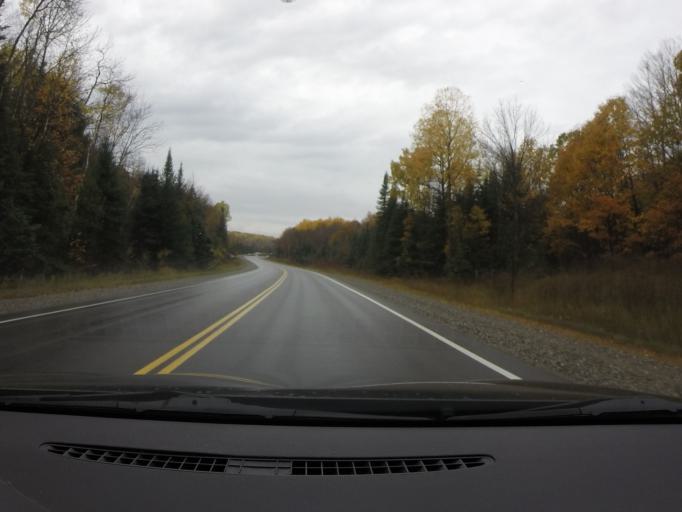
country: CA
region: Ontario
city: Perth
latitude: 44.7642
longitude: -76.7634
